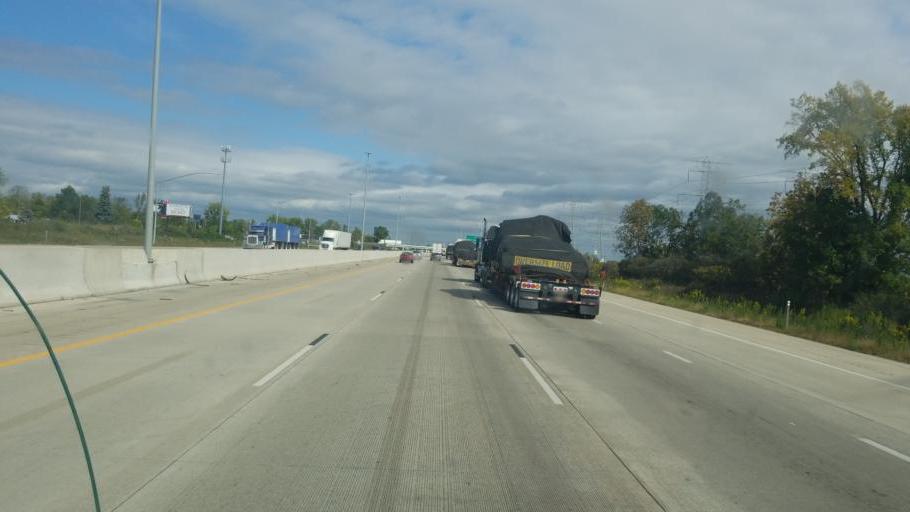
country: US
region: Michigan
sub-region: Monroe County
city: Detroit Beach
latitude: 41.9210
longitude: -83.3616
